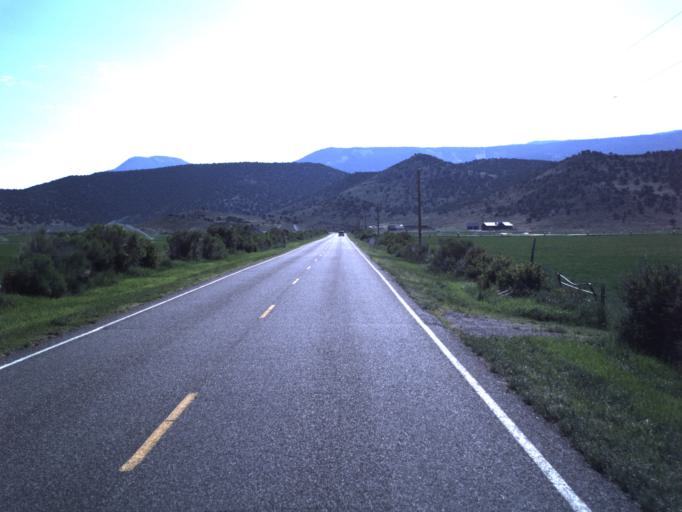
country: US
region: Utah
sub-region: Wayne County
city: Loa
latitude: 38.4694
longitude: -111.5862
